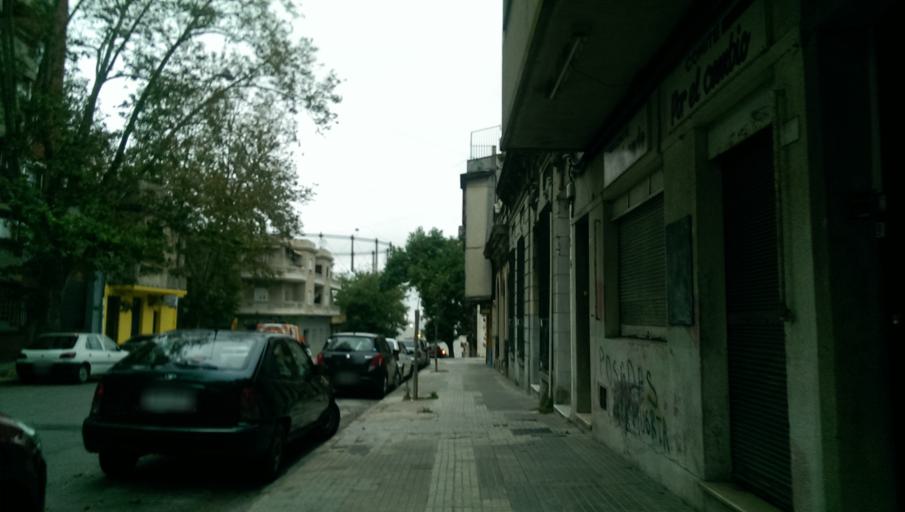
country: UY
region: Montevideo
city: Montevideo
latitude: -34.9101
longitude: -56.1945
